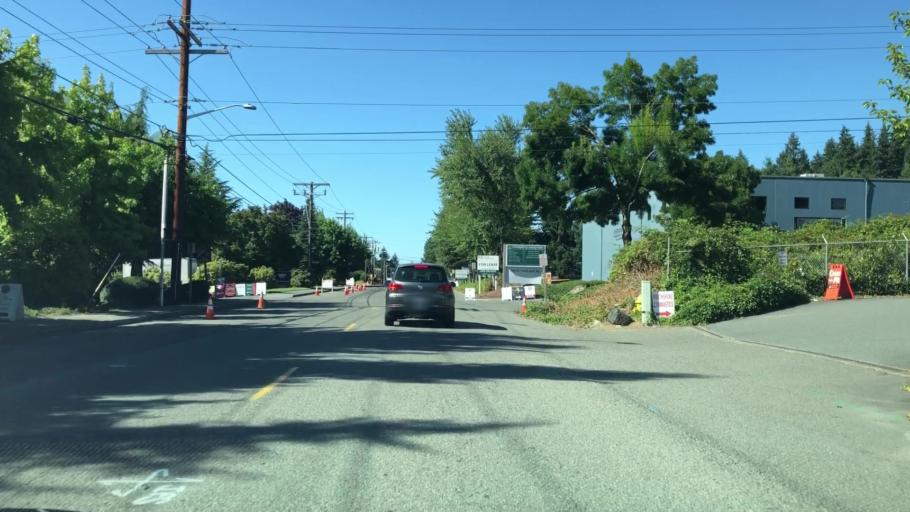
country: US
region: Washington
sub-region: King County
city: Woodinville
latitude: 47.7685
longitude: -122.1478
